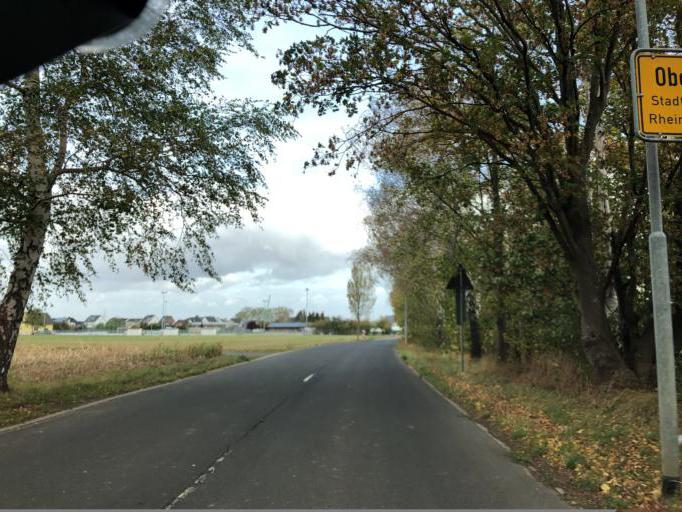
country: DE
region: North Rhine-Westphalia
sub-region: Regierungsbezirk Koln
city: Rheinbach
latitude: 50.6352
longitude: 6.9175
